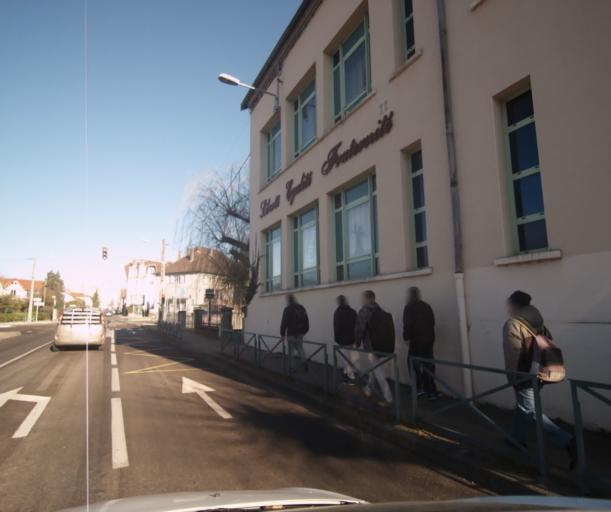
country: FR
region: Franche-Comte
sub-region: Departement du Doubs
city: Besancon
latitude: 47.2369
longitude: 6.0069
